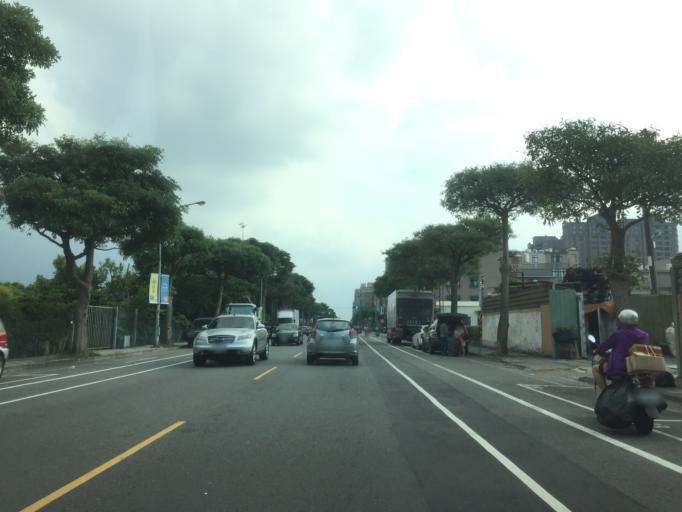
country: TW
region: Taiwan
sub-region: Taoyuan
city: Taoyuan
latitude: 24.9689
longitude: 121.3068
